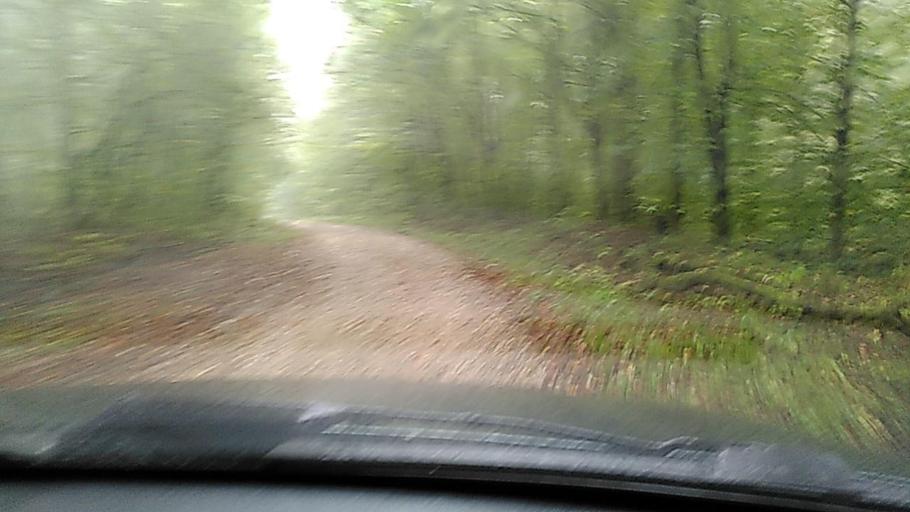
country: RU
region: Kabardino-Balkariya
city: Belaya Rechka
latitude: 43.3700
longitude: 43.4241
